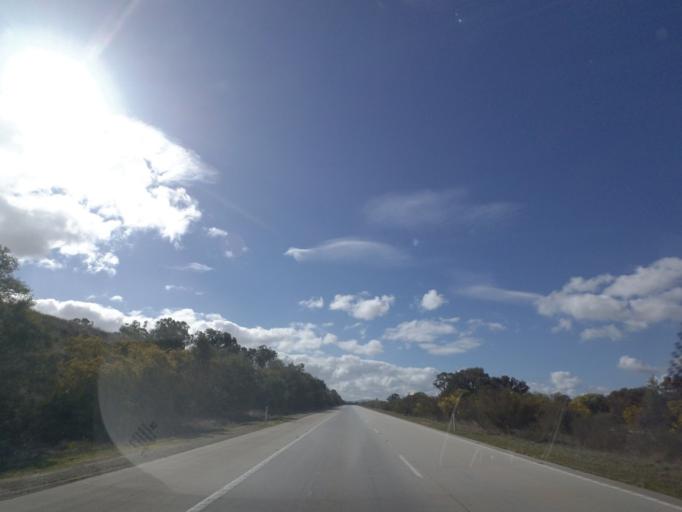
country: AU
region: New South Wales
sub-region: Albury Municipality
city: Lavington
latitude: -36.0145
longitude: 146.9861
